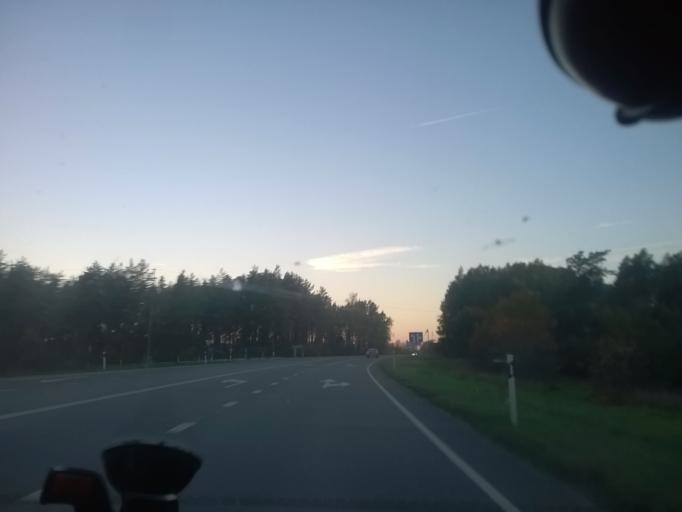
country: EE
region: Laeaene
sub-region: Ridala Parish
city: Uuemoisa
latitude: 58.9567
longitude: 23.7269
